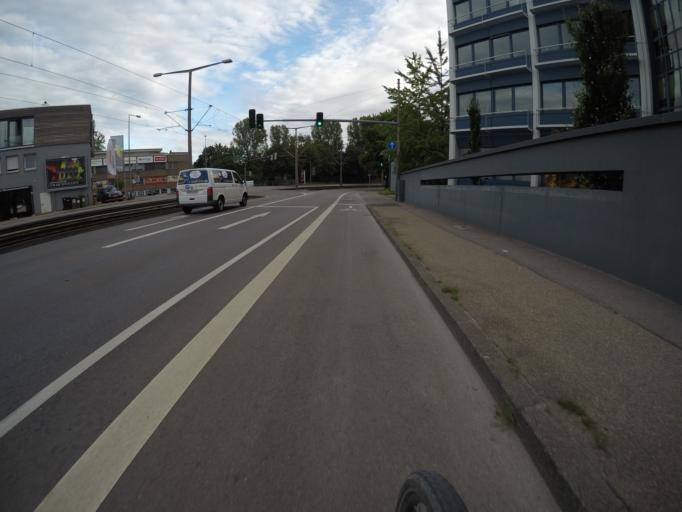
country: DE
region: Baden-Wuerttemberg
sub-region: Regierungsbezirk Stuttgart
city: Stuttgart-Ost
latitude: 48.8113
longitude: 9.2164
